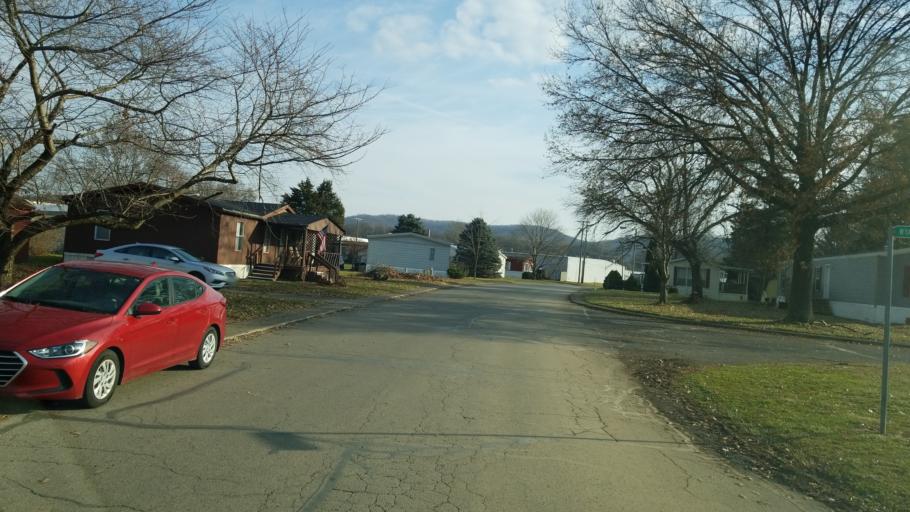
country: US
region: Ohio
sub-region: Ross County
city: Chillicothe
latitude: 39.3634
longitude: -82.9815
